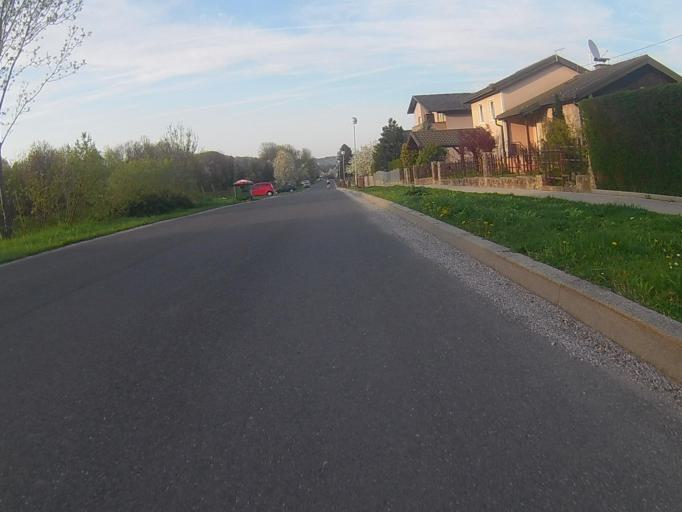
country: SI
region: Maribor
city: Pekre
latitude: 46.5427
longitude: 15.5911
